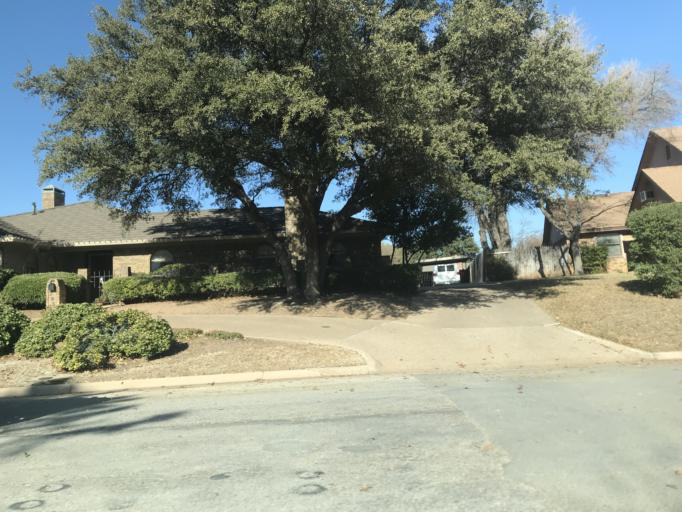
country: US
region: Texas
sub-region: Taylor County
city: Abilene
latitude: 32.3835
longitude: -99.7630
